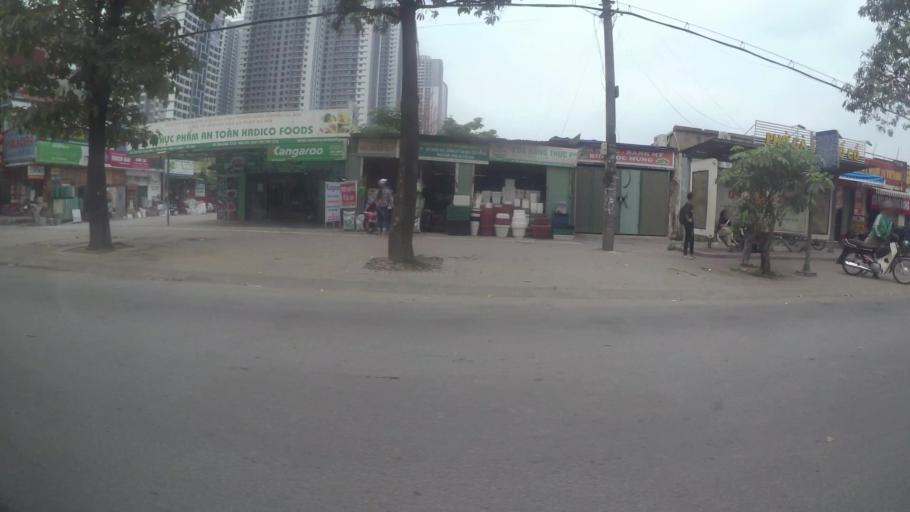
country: VN
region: Ha Noi
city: Cau Dien
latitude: 21.0399
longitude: 105.7669
